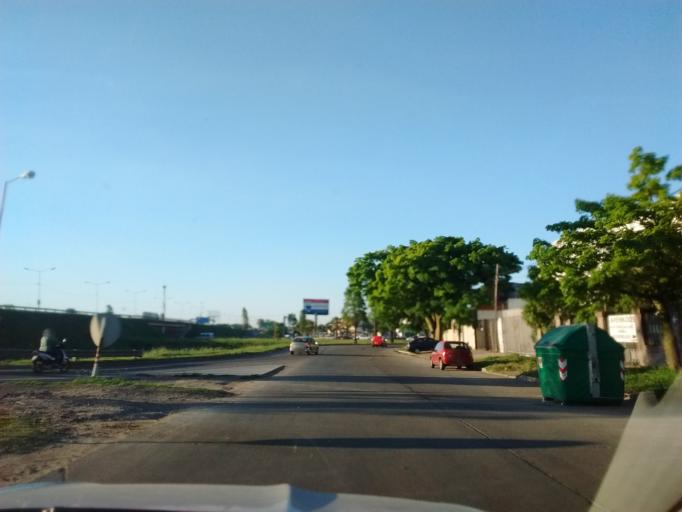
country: AR
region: Santa Fe
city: Granadero Baigorria
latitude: -32.9329
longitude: -60.7223
